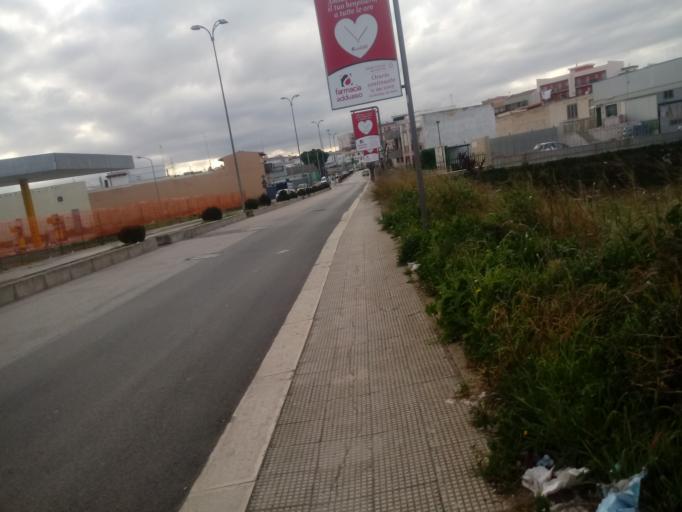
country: IT
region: Apulia
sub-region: Provincia di Barletta - Andria - Trani
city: Andria
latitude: 41.2175
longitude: 16.2983
